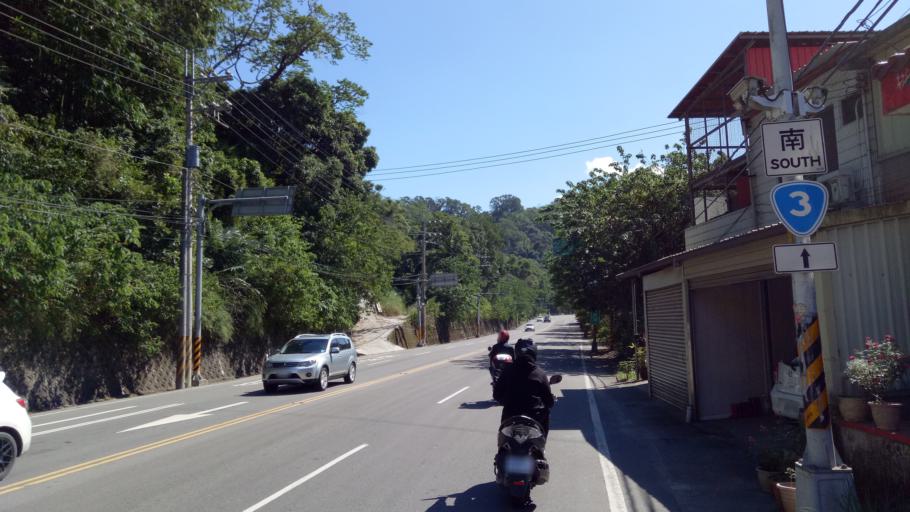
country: TW
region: Taiwan
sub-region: Hsinchu
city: Hsinchu
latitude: 24.6819
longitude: 120.9641
